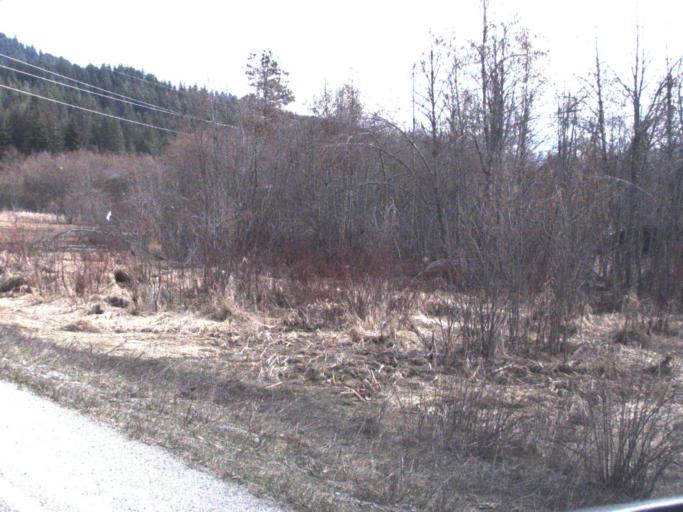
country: US
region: Washington
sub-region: Pend Oreille County
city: Newport
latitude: 48.4666
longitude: -117.3223
